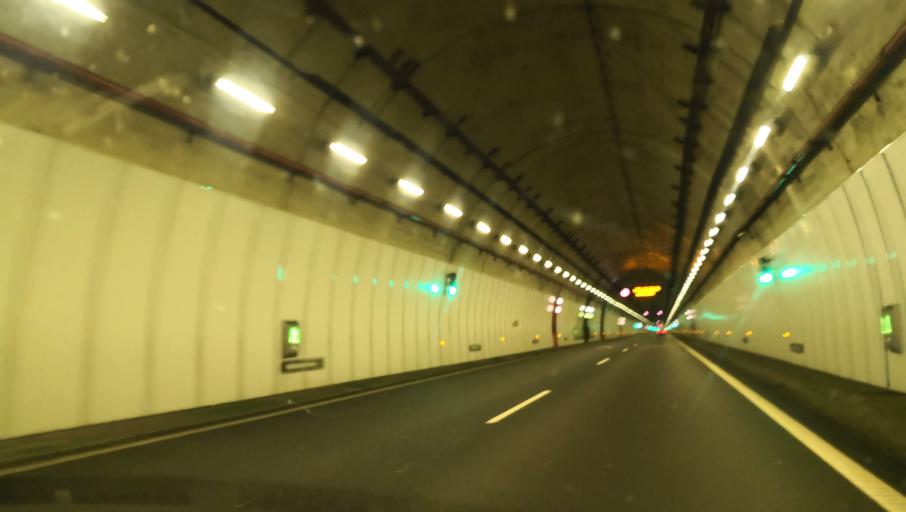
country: ES
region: Galicia
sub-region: Provincia de Pontevedra
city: Covelo
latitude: 42.1795
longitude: -8.3401
